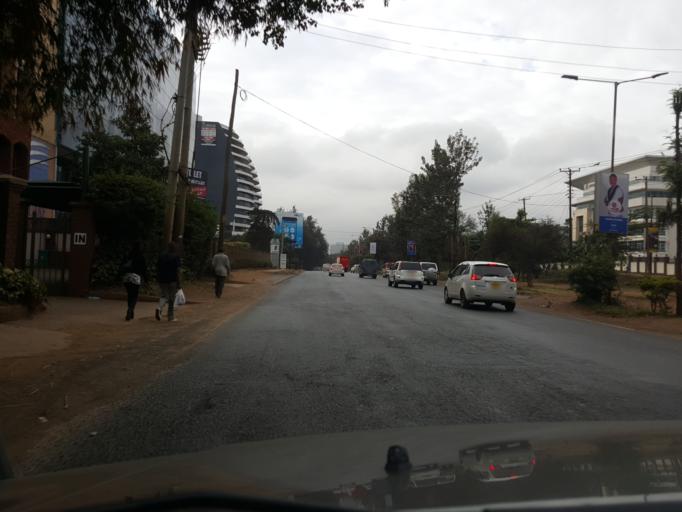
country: KE
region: Nairobi Area
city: Nairobi
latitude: -1.2682
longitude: 36.8054
